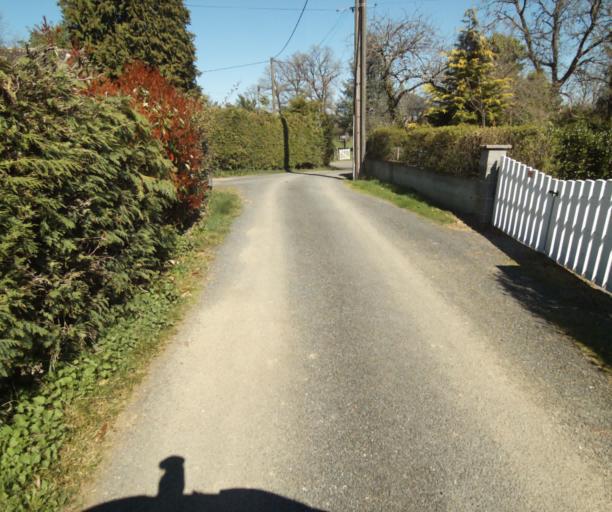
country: FR
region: Limousin
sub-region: Departement de la Correze
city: Saint-Clement
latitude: 45.3201
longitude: 1.6672
